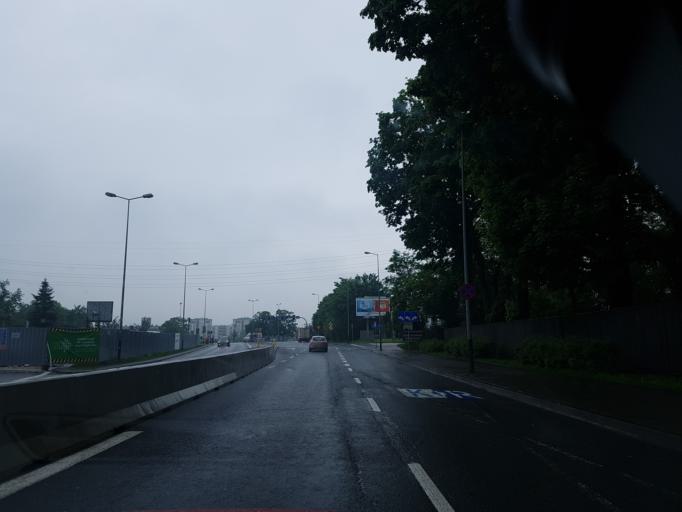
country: PL
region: Lesser Poland Voivodeship
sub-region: Krakow
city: Krakow
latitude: 50.0528
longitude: 19.9538
